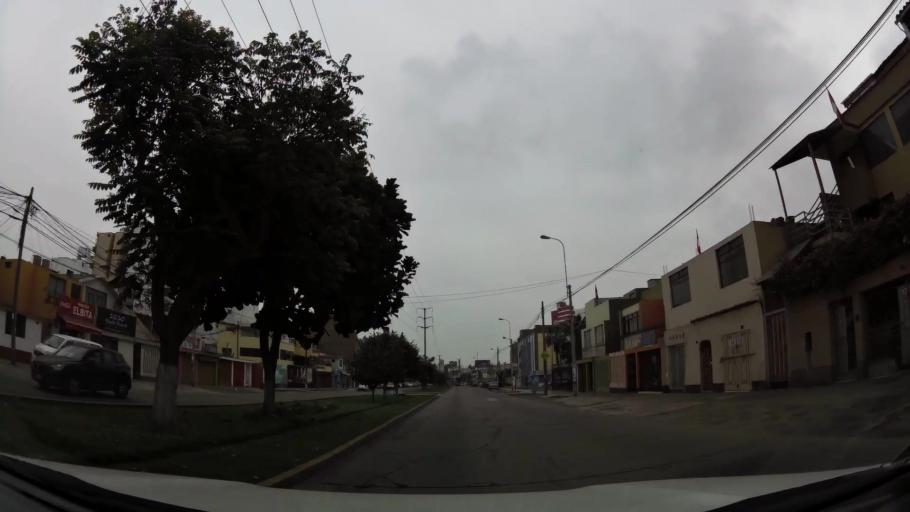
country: PE
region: Lima
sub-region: Lima
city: Surco
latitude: -12.1203
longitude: -77.0012
